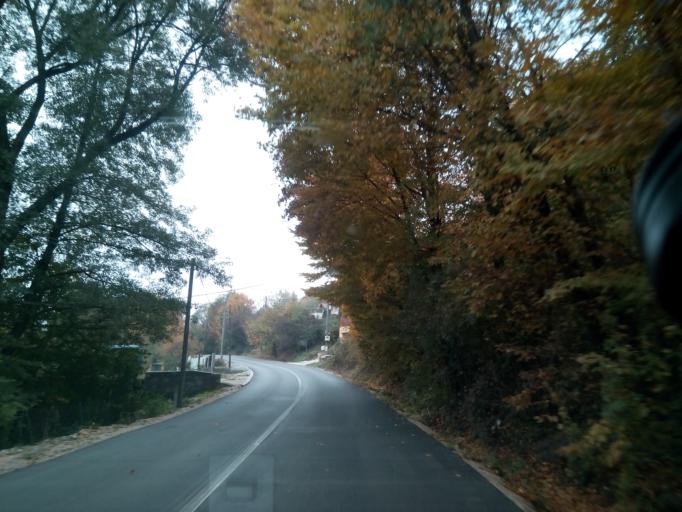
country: SK
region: Kosicky
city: Kosice
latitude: 48.7244
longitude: 21.1574
